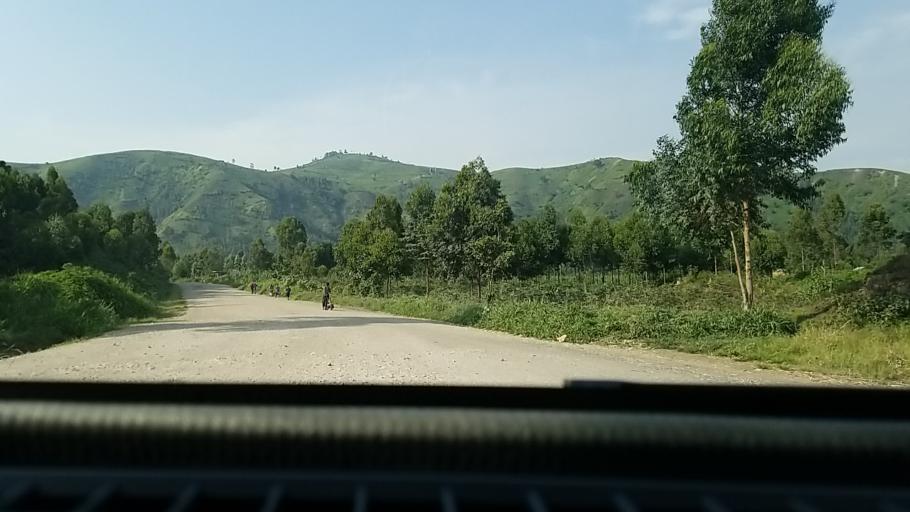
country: CD
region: Nord Kivu
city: Sake
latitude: -1.5714
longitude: 29.0466
